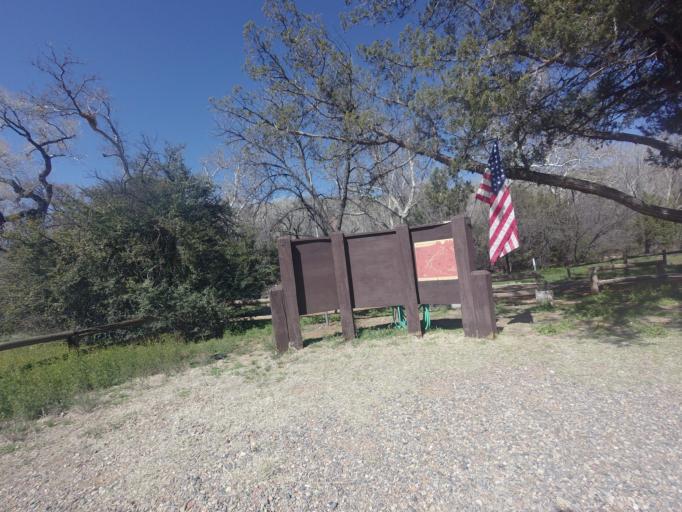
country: US
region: Arizona
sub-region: Yavapai County
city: Lake Montezuma
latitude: 34.6661
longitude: -111.7169
